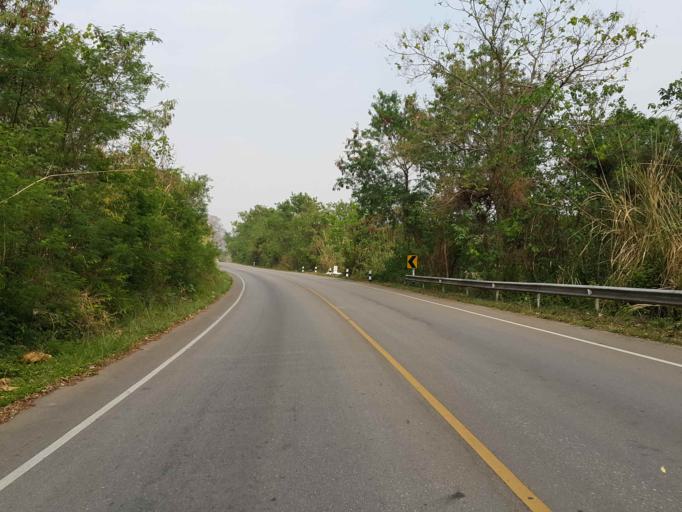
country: TH
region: Chiang Mai
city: Mae Taeng
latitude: 19.0994
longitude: 99.0743
